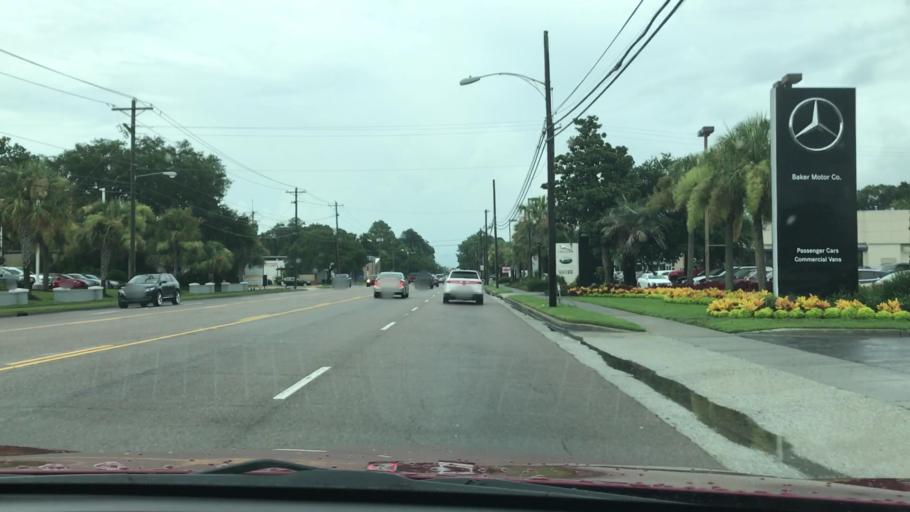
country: US
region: South Carolina
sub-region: Charleston County
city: Charleston
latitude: 32.7852
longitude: -80.0042
